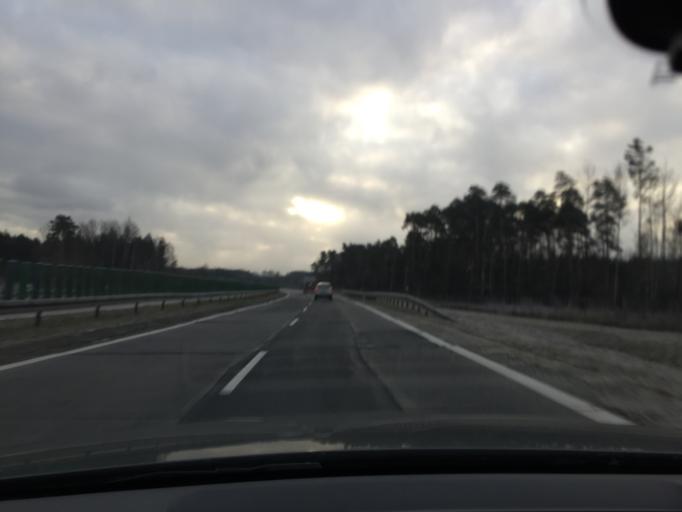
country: PL
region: Lubusz
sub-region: Powiat zarski
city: Sieniawa Zarska
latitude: 51.5720
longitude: 15.0351
